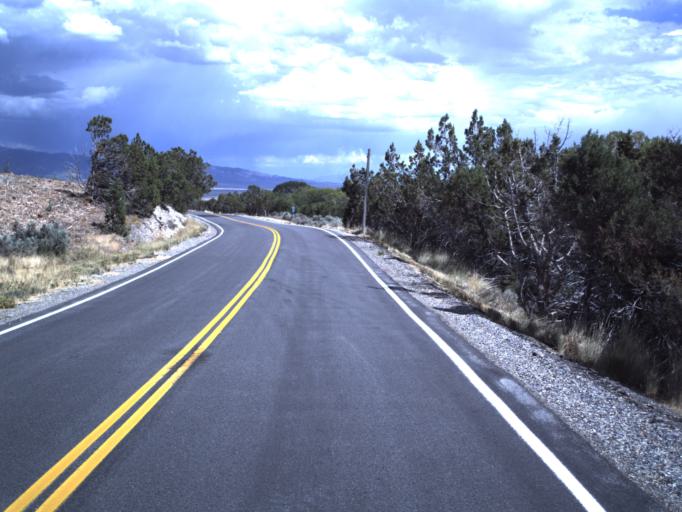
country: US
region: Utah
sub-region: Tooele County
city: Grantsville
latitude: 40.3329
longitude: -112.5207
